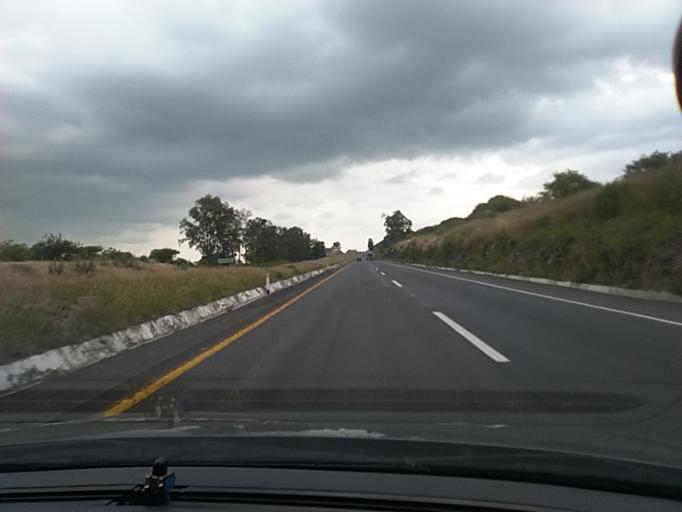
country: MX
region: Jalisco
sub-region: Poncitlan
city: Santa Cruz el Grande
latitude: 20.4430
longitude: -102.8419
